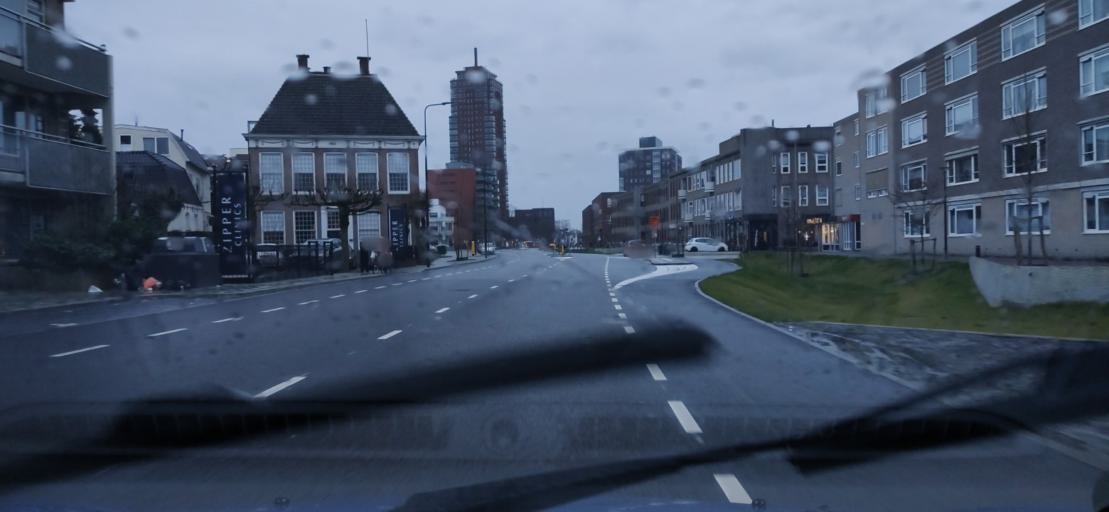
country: NL
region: Overijssel
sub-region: Gemeente Enschede
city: Enschede
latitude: 52.2203
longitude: 6.9001
